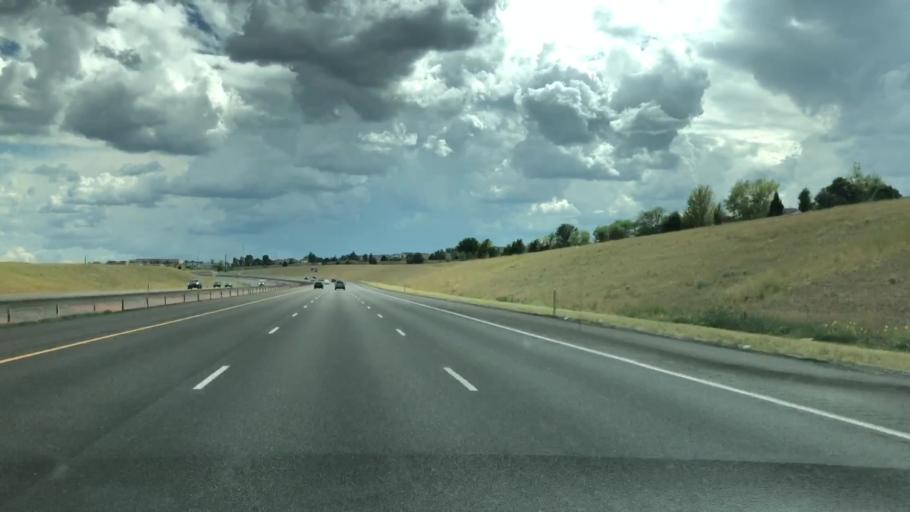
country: US
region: Colorado
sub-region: Douglas County
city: Parker
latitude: 39.6228
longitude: -104.7186
